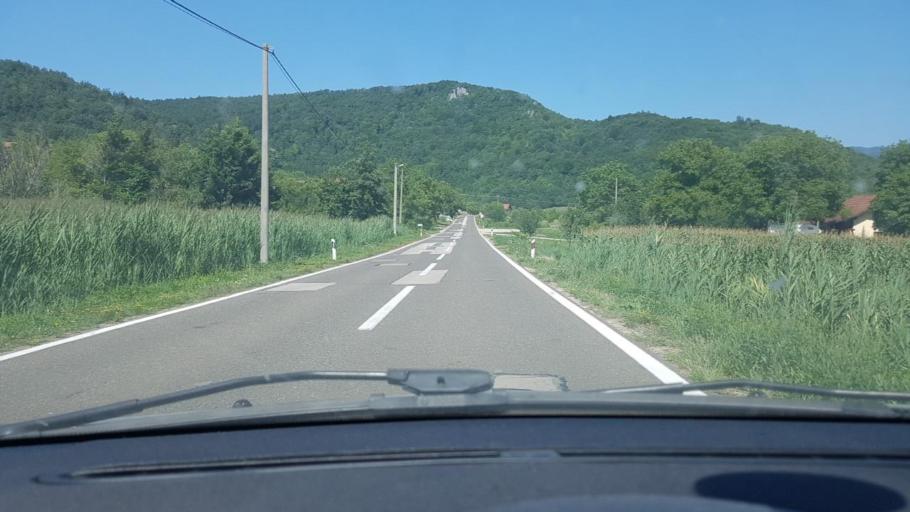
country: BA
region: Federation of Bosnia and Herzegovina
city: Bihac
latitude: 44.7488
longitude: 15.9259
